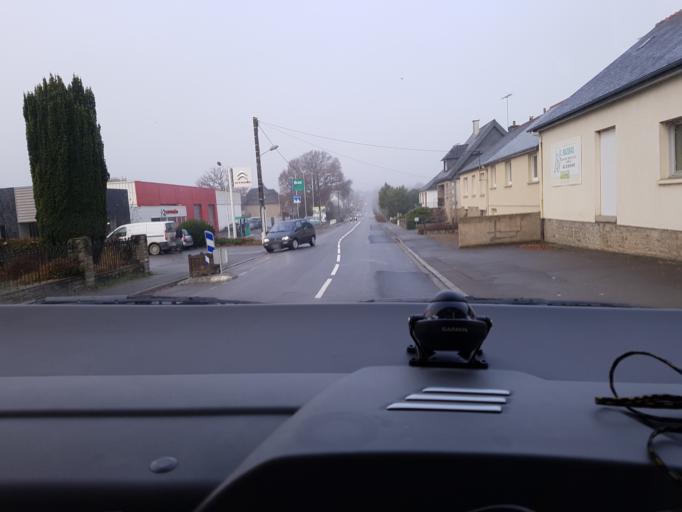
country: FR
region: Brittany
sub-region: Departement d'Ille-et-Vilaine
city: Livre-sur-Changeon
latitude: 48.1785
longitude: -1.3090
